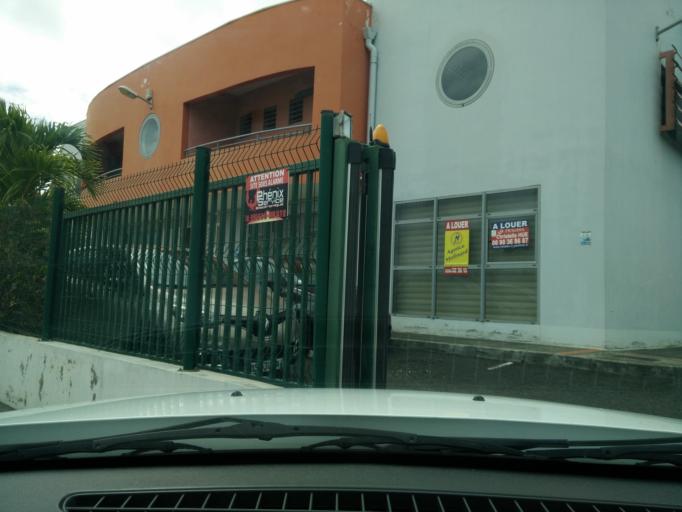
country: GP
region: Guadeloupe
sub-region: Guadeloupe
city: Petit-Bourg
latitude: 16.2026
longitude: -61.6084
